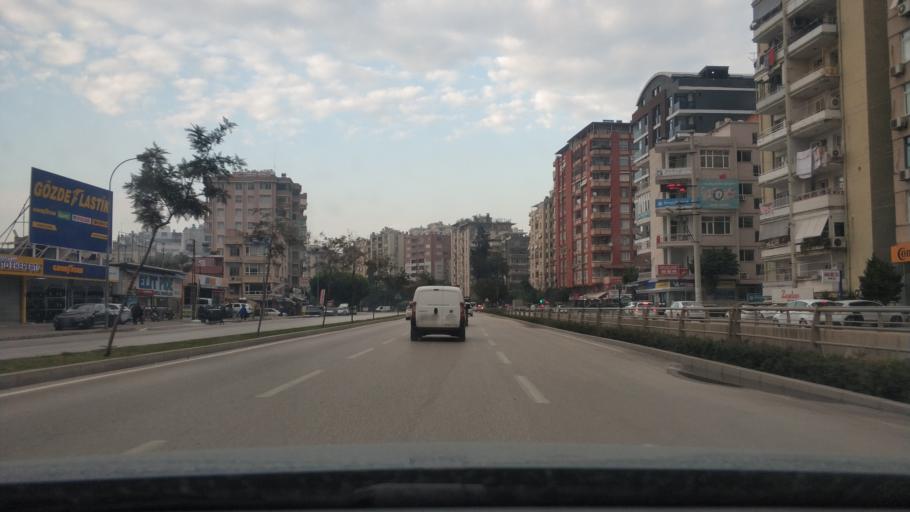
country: TR
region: Adana
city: Adana
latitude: 36.9956
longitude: 35.3182
